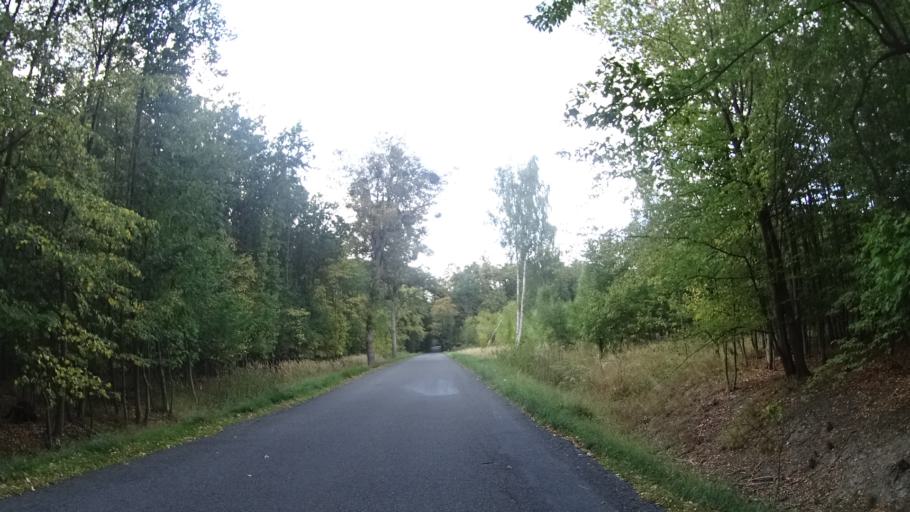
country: CZ
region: Olomoucky
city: Bila Lhota
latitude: 49.7276
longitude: 17.0151
